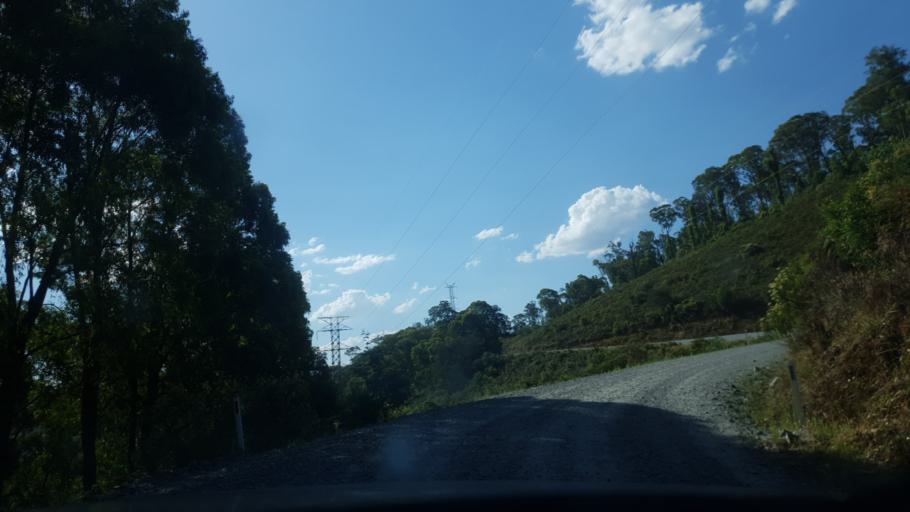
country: AU
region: Victoria
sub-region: Alpine
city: Mount Beauty
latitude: -36.7507
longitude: 147.1828
